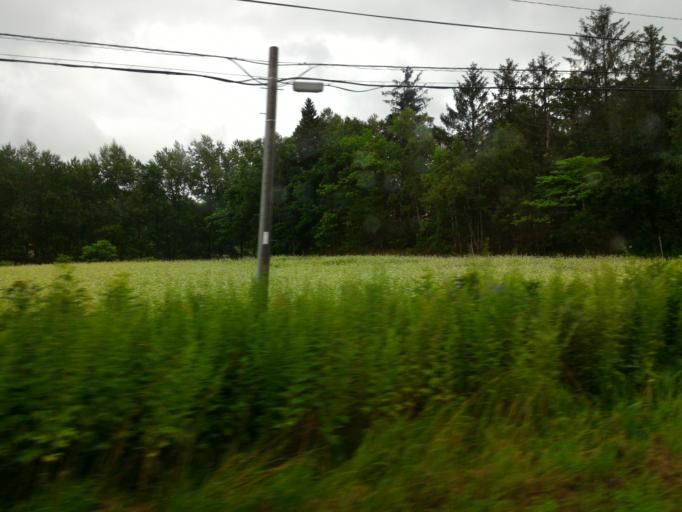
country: JP
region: Hokkaido
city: Nayoro
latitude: 44.6673
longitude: 142.2684
